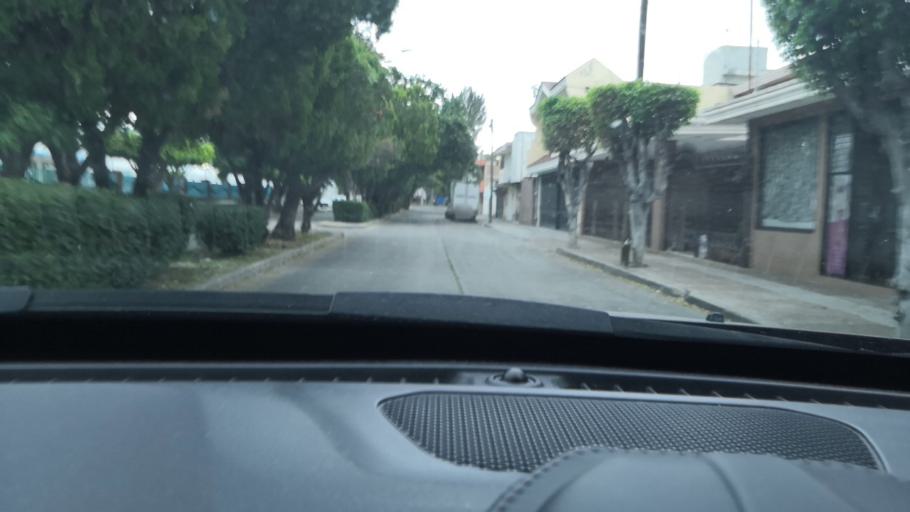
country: MX
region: Guanajuato
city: Leon
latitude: 21.1113
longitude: -101.6689
